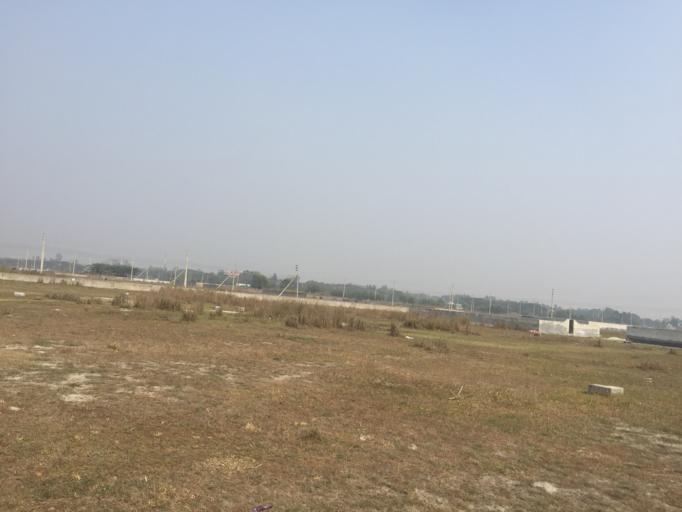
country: BD
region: Dhaka
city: Tungi
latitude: 23.8656
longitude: 90.3152
